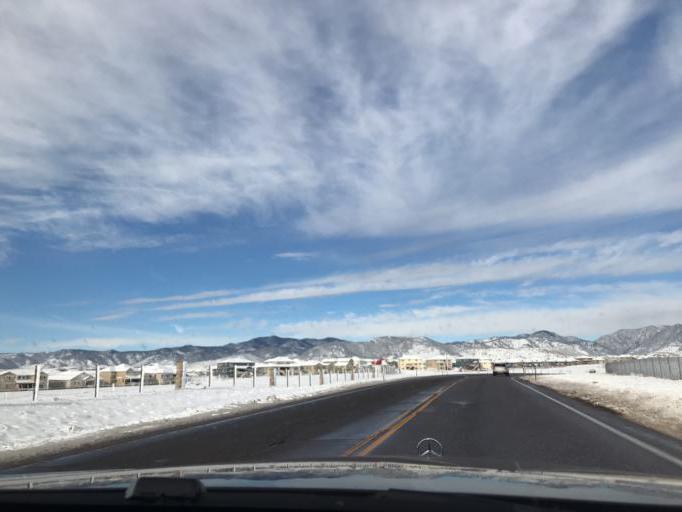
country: US
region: Colorado
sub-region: Jefferson County
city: Applewood
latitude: 39.8516
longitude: -105.1769
